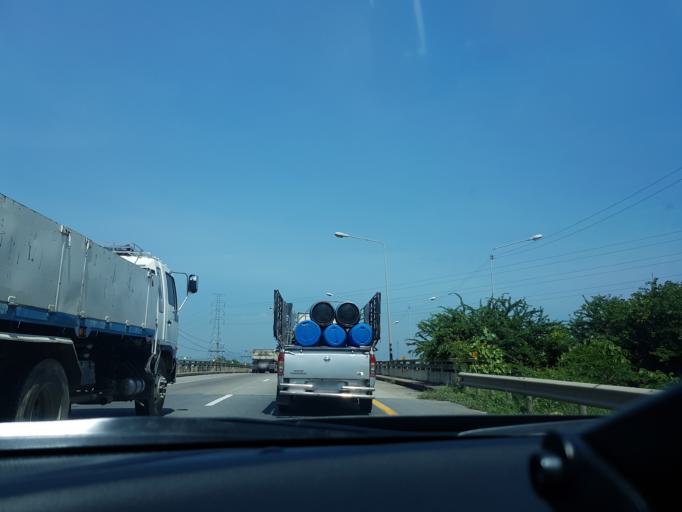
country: TH
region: Sara Buri
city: Saraburi
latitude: 14.5243
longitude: 100.8884
